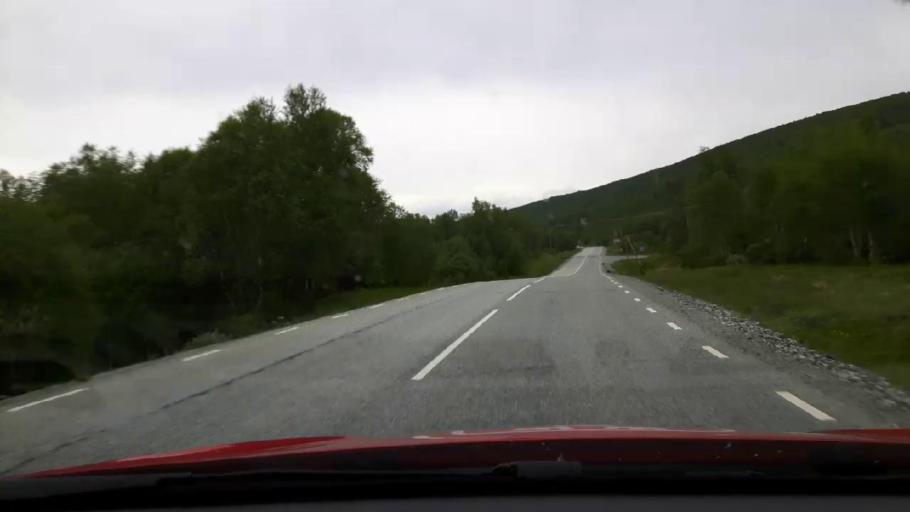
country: NO
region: Sor-Trondelag
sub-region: Tydal
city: Aas
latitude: 62.6599
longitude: 12.4278
